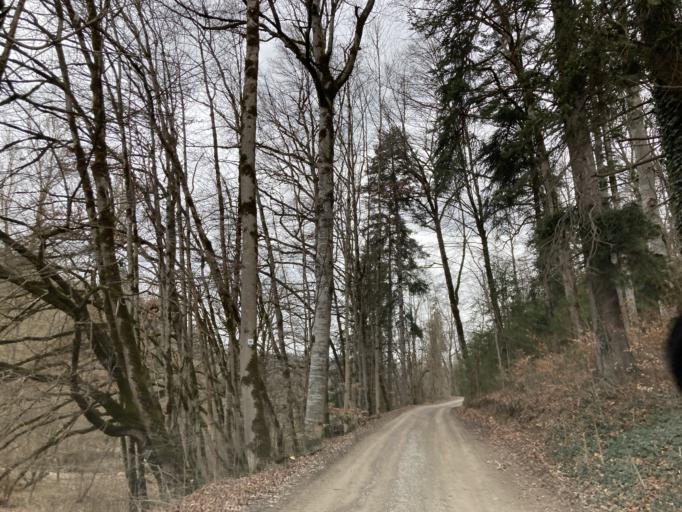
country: DE
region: Baden-Wuerttemberg
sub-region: Tuebingen Region
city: Hirrlingen
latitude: 48.4203
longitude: 8.8654
